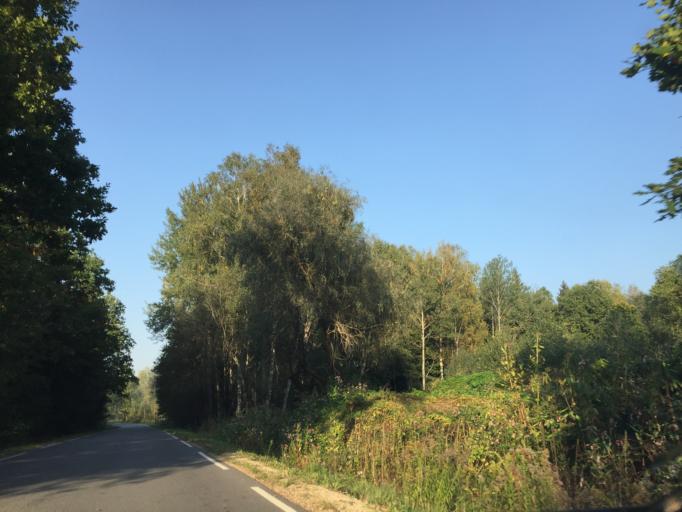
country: LV
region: Kegums
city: Kegums
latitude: 56.8106
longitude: 24.7462
